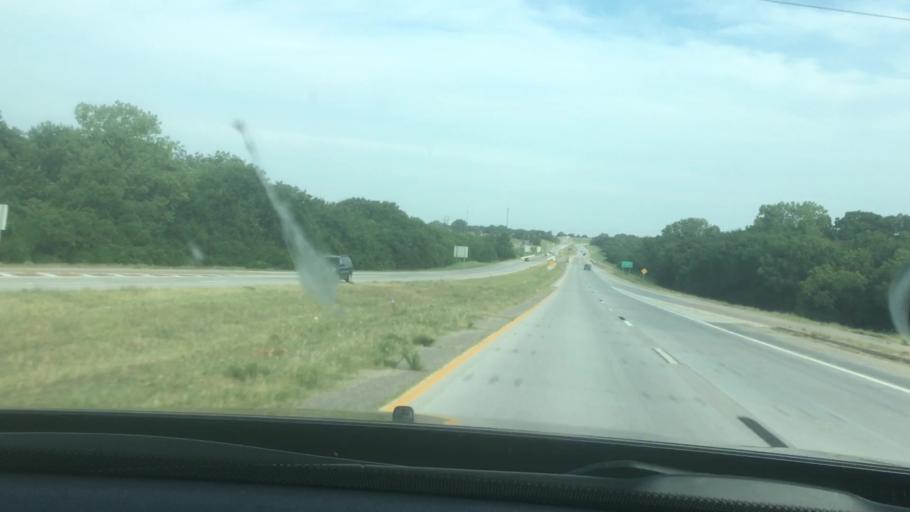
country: US
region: Oklahoma
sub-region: Pontotoc County
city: Ada
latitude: 34.7775
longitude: -96.7051
